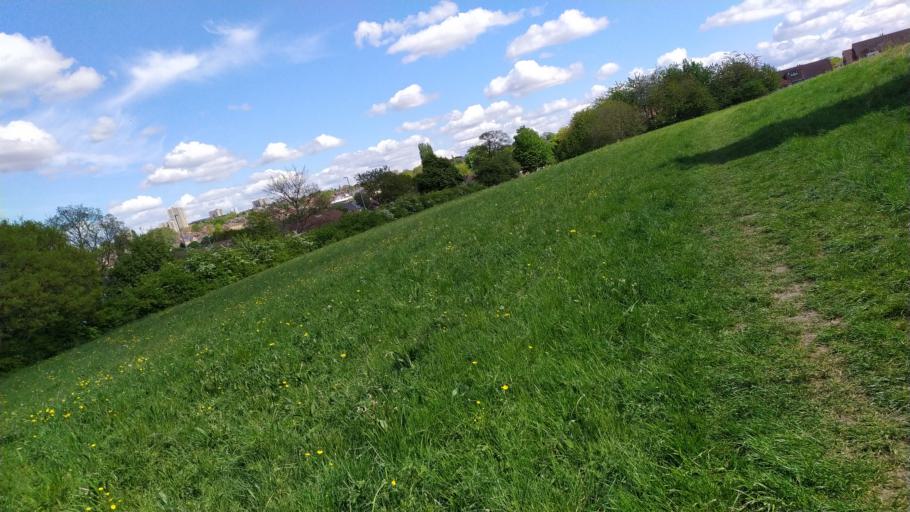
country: GB
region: England
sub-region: City and Borough of Leeds
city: Shadwell
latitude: 53.8110
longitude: -1.4791
